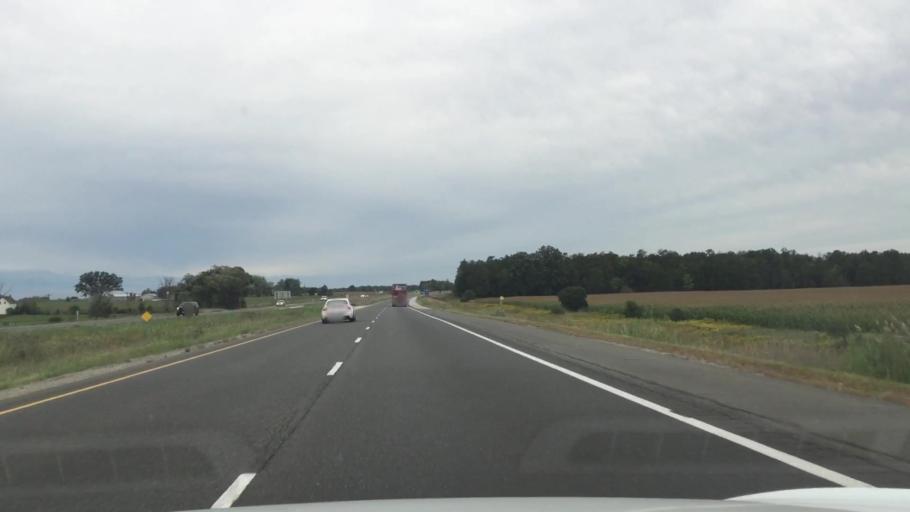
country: CA
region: Ontario
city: Delaware
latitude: 42.8895
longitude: -81.3045
